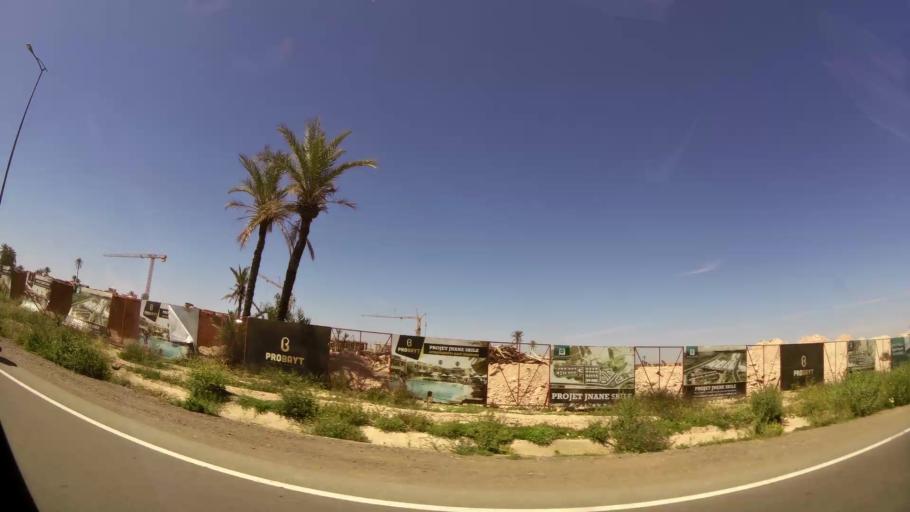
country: MA
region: Marrakech-Tensift-Al Haouz
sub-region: Marrakech
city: Marrakesh
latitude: 31.6739
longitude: -7.9907
